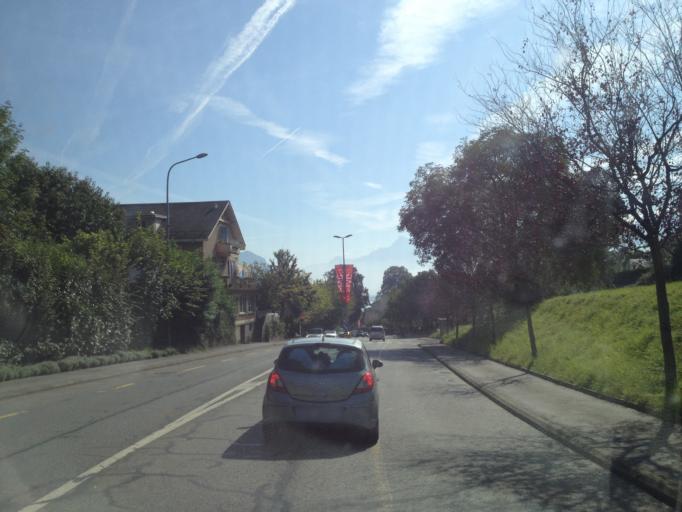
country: CH
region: Vaud
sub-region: Riviera-Pays-d'Enhaut District
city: Le Chatelard
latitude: 46.4490
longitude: 6.8917
